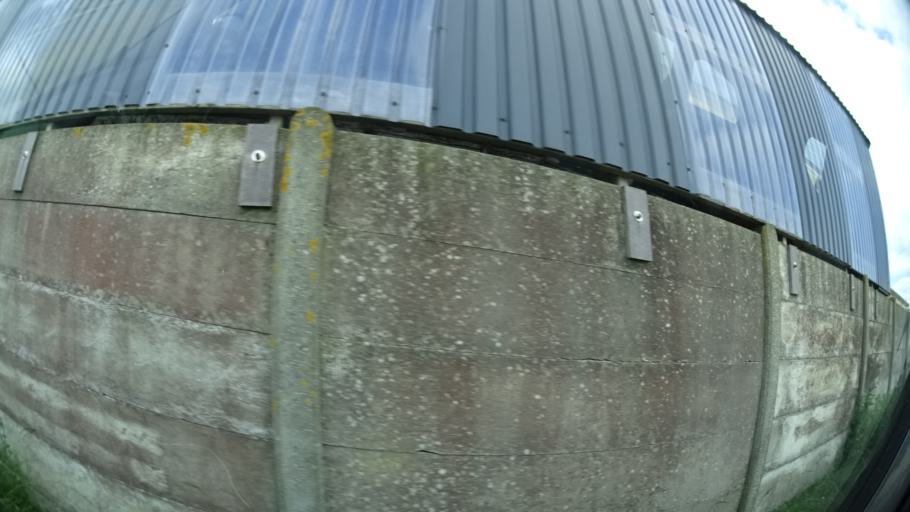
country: DK
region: Central Jutland
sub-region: Norddjurs Kommune
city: Grenaa
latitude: 56.5322
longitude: 10.7149
